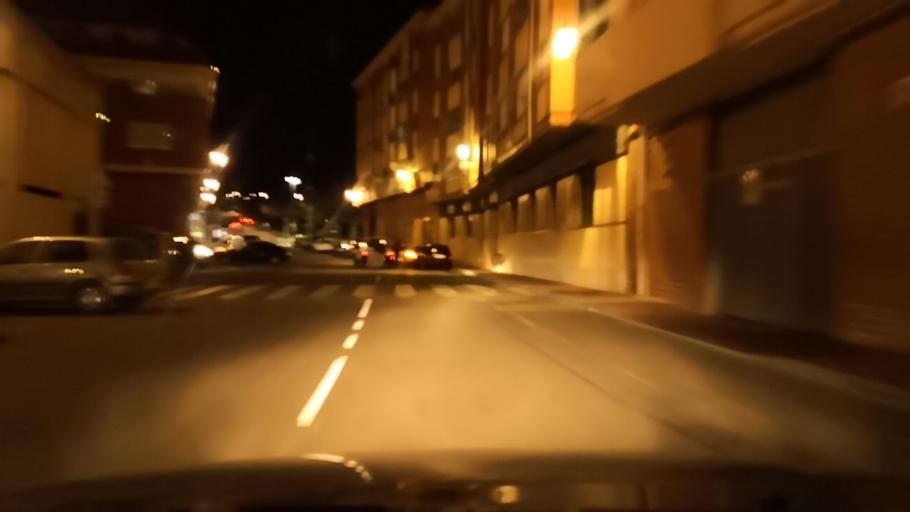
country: ES
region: Castille and Leon
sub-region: Provincia de Zamora
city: Benavente
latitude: 42.0065
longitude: -5.6838
